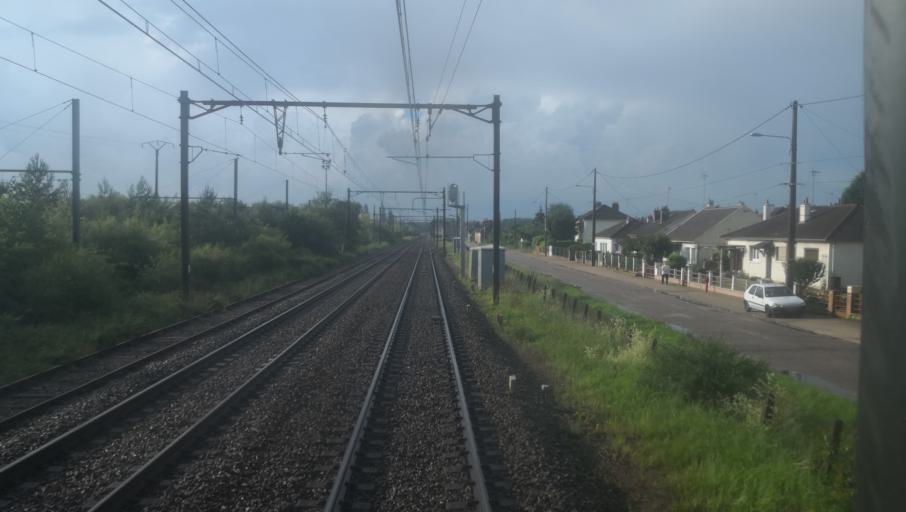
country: FR
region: Centre
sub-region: Departement du Loiret
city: La Ferte-Saint-Aubin
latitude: 47.7159
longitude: 1.9337
